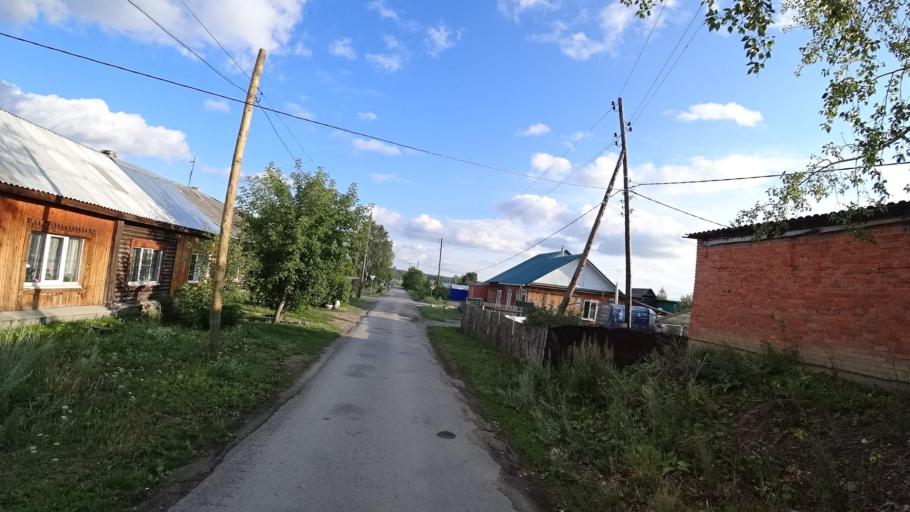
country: RU
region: Sverdlovsk
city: Kamyshlov
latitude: 56.8497
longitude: 62.6647
